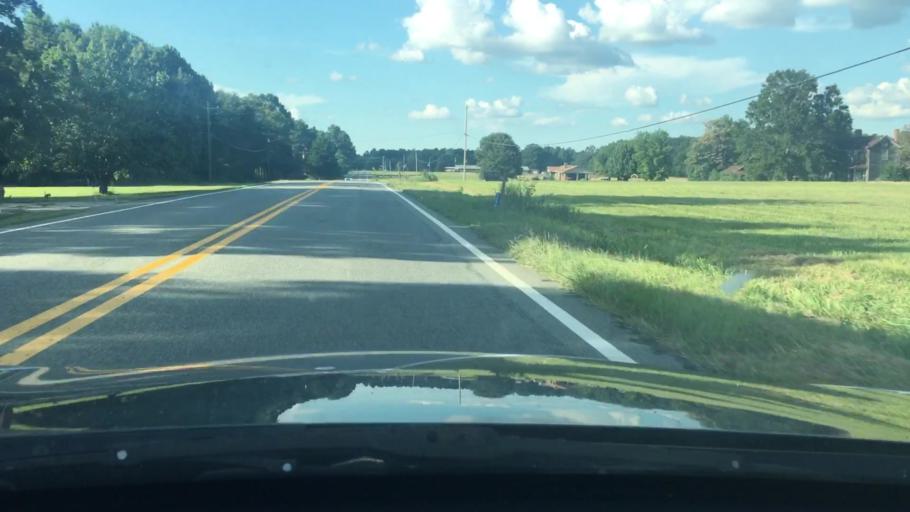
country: US
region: North Carolina
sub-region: Alamance County
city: Green Level
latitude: 36.1812
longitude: -79.3284
